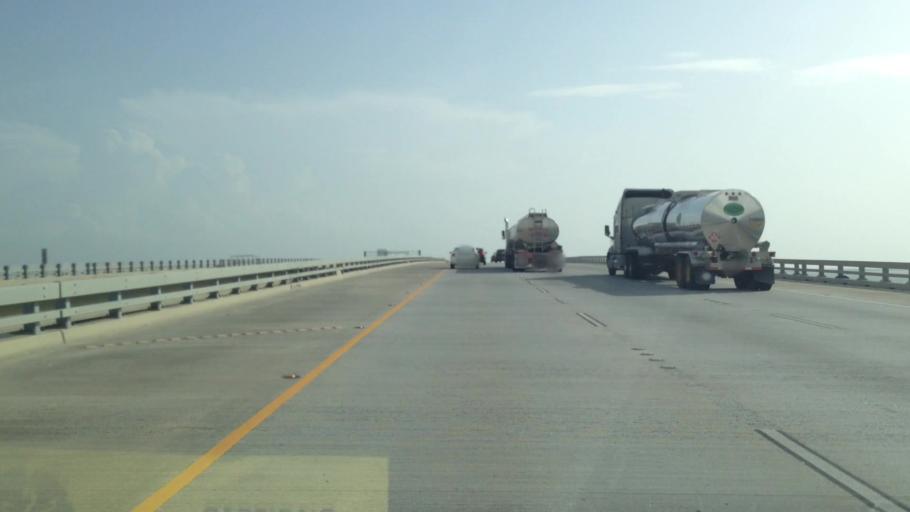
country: US
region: Louisiana
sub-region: Saint Tammany Parish
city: Eden Isle
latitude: 30.1987
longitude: -89.8070
